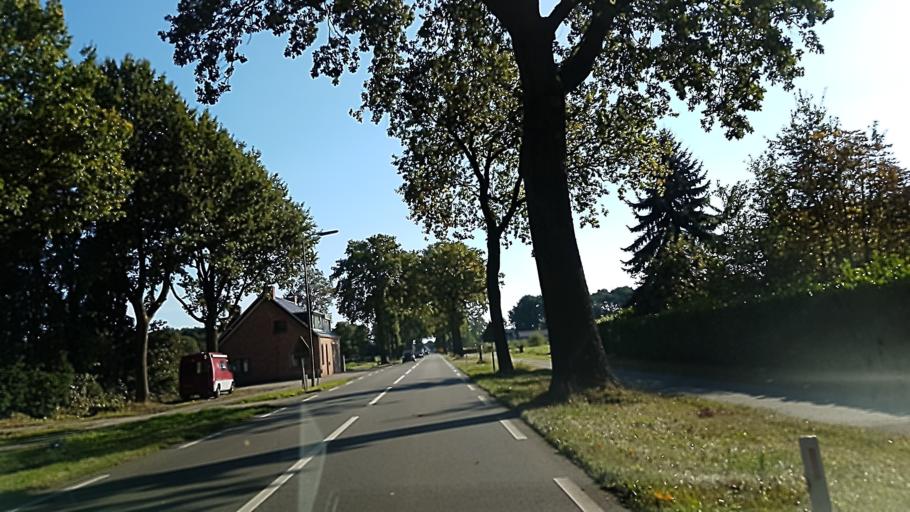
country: BE
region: Flanders
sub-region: Provincie Antwerpen
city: Stabroek
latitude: 51.3698
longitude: 4.3869
